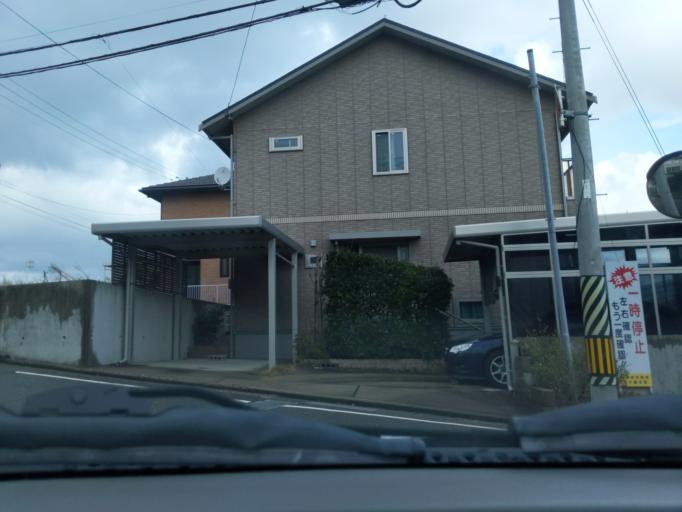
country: JP
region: Niigata
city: Niigata-shi
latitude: 37.9322
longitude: 139.0432
